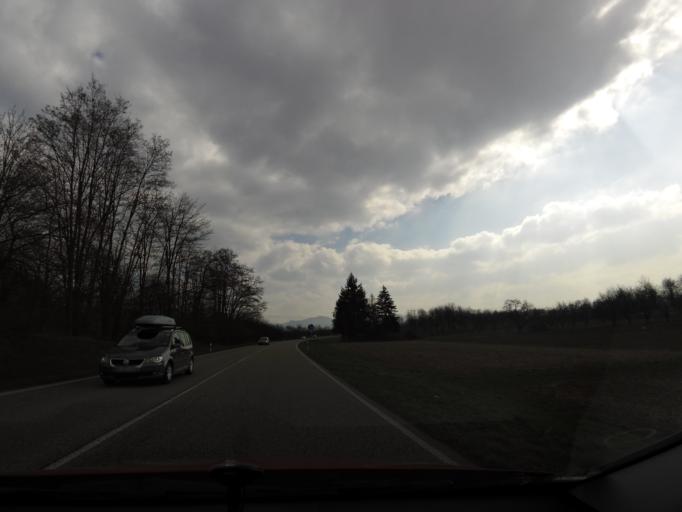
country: DE
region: Baden-Wuerttemberg
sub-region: Freiburg Region
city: Achern
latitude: 48.6199
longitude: 8.0642
